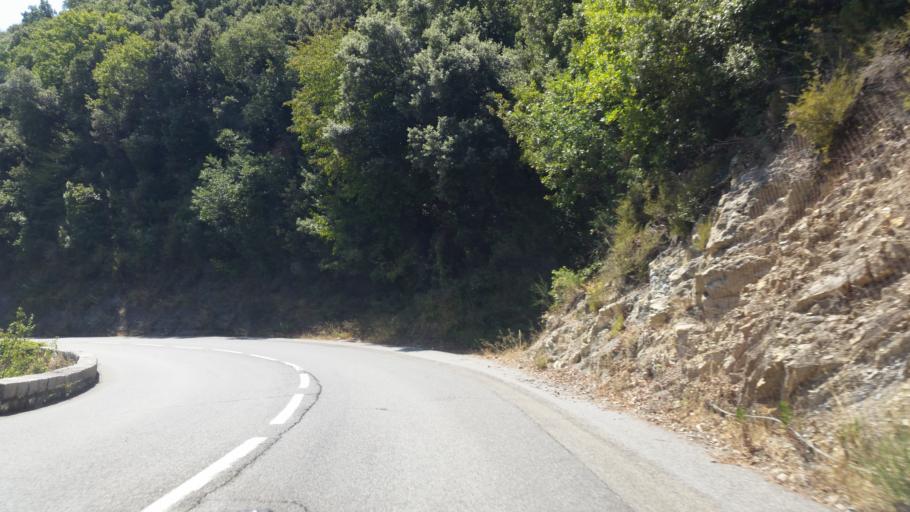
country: FR
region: Provence-Alpes-Cote d'Azur
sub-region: Departement des Alpes-Maritimes
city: Sainte-Agnes
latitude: 43.8225
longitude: 7.4827
